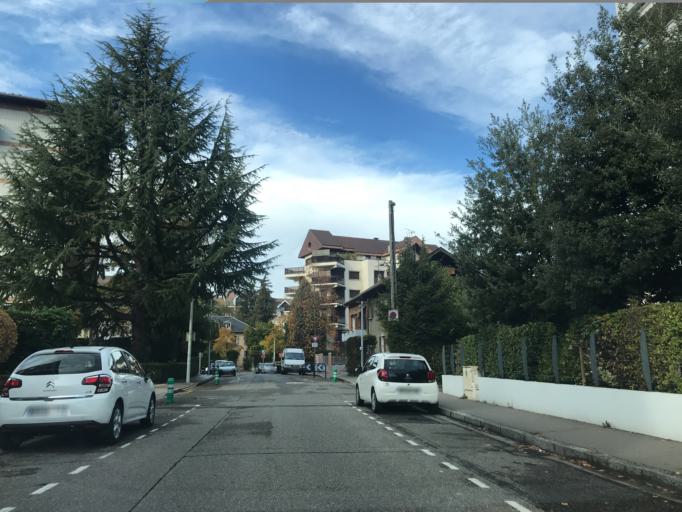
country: FR
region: Rhone-Alpes
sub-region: Departement de la Haute-Savoie
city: Annecy-le-Vieux
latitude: 45.9064
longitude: 6.1357
